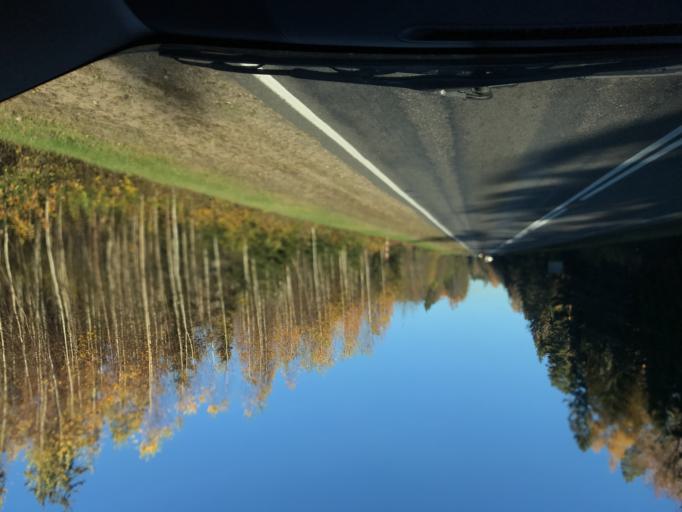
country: BY
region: Vitebsk
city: Polatsk
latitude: 55.4153
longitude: 28.7956
